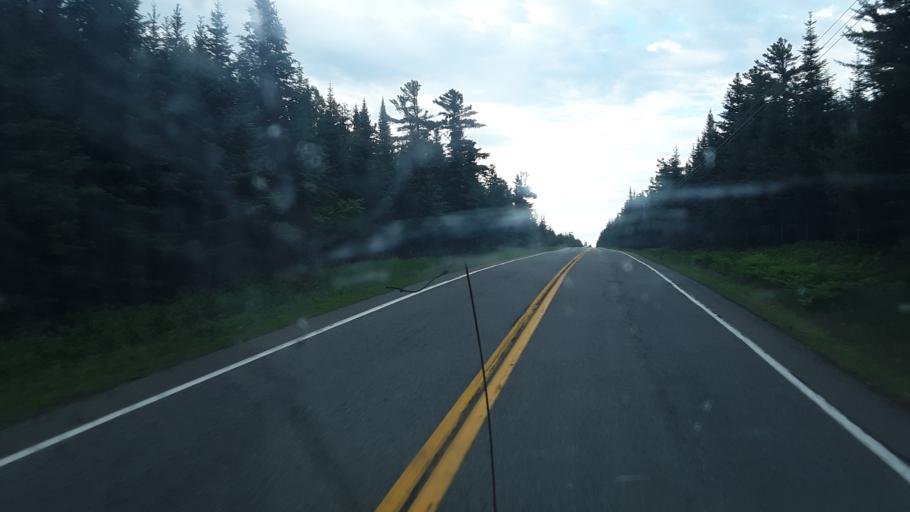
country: US
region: Maine
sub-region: Penobscot County
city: Patten
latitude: 46.4085
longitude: -68.3670
